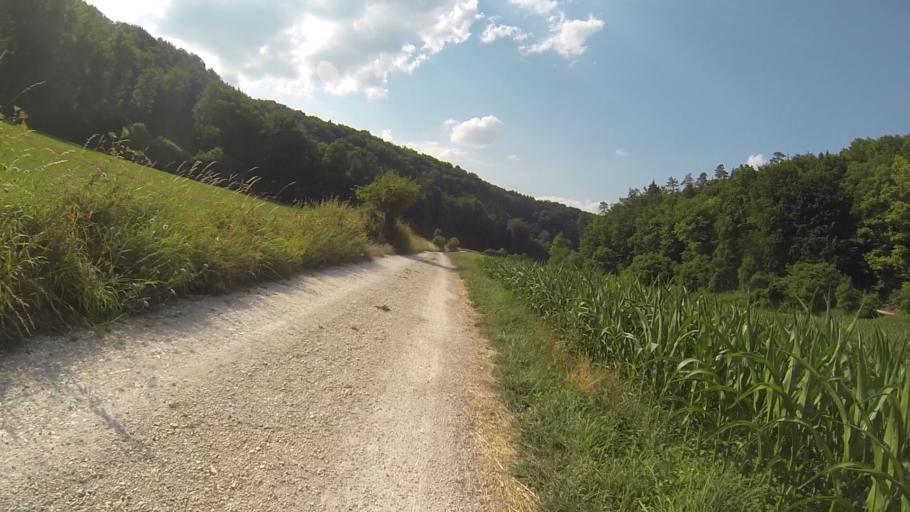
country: DE
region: Baden-Wuerttemberg
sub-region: Tuebingen Region
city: Dornstadt
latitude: 48.4316
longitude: 9.9064
